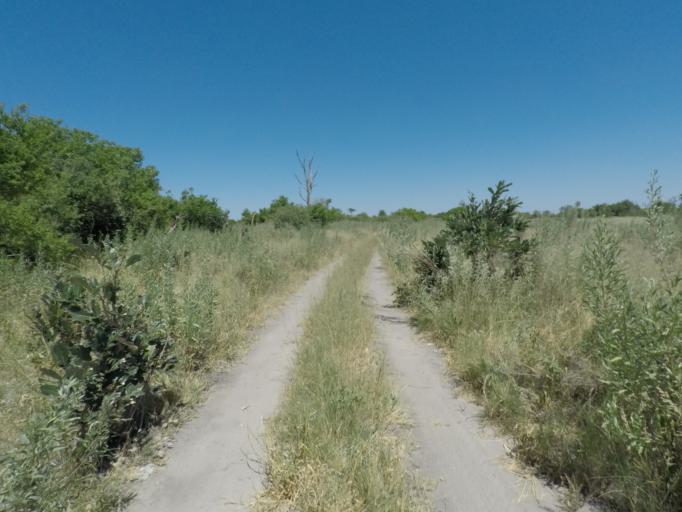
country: BW
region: North West
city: Maun
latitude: -19.4738
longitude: 23.5530
